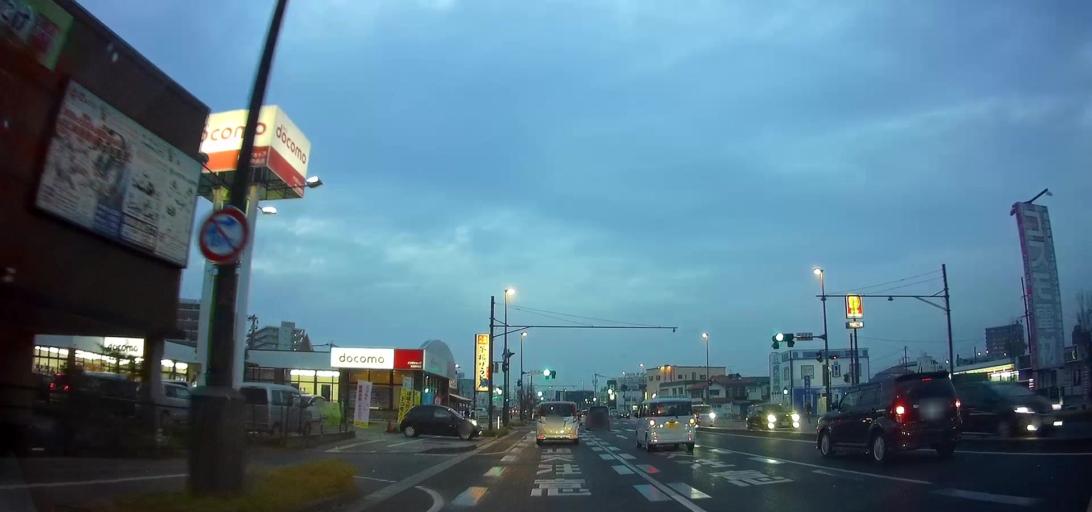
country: JP
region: Nagasaki
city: Omura
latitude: 32.9045
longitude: 129.9575
